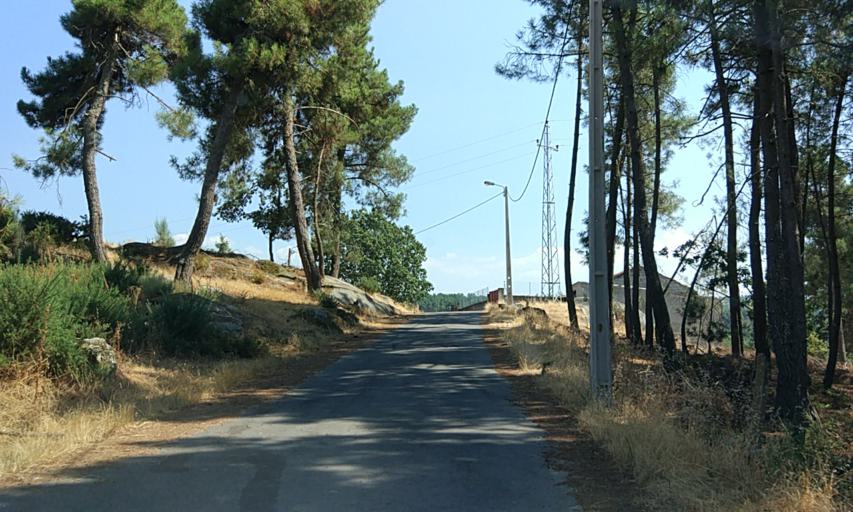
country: PT
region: Vila Real
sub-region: Murca
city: Murca
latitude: 41.3504
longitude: -7.4856
